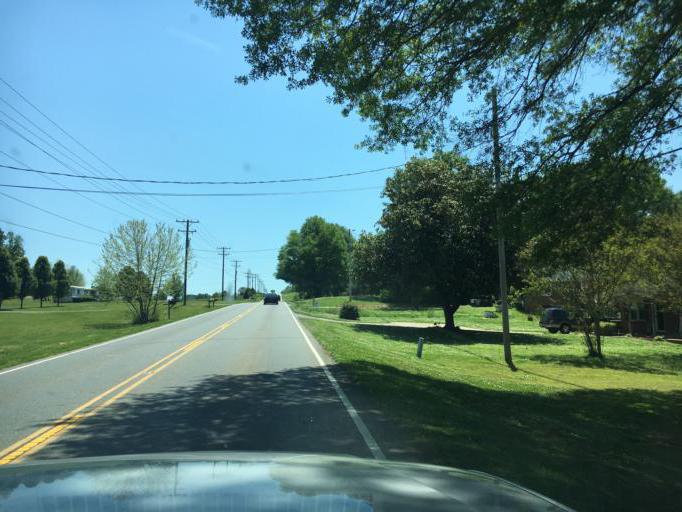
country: US
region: North Carolina
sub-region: Cleveland County
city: Shelby
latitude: 35.2385
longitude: -81.5664
